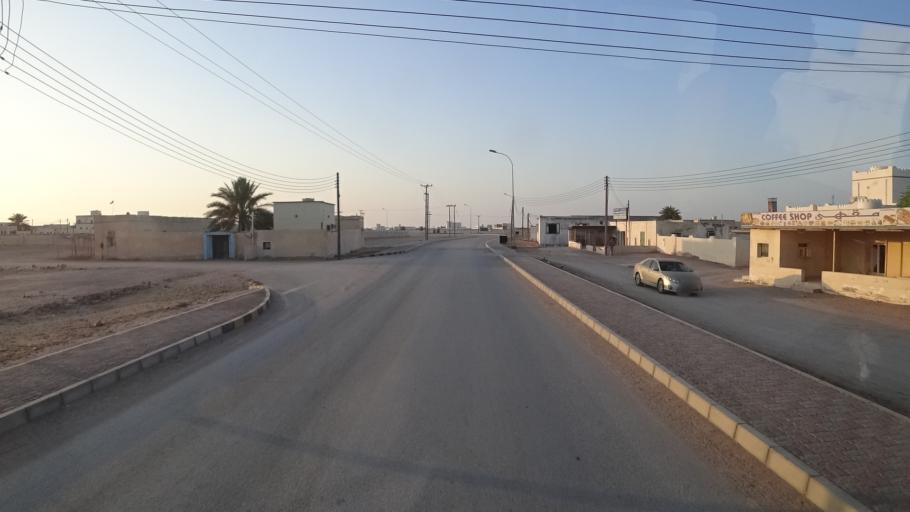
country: OM
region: Ash Sharqiyah
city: Sur
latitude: 22.5238
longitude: 59.7920
